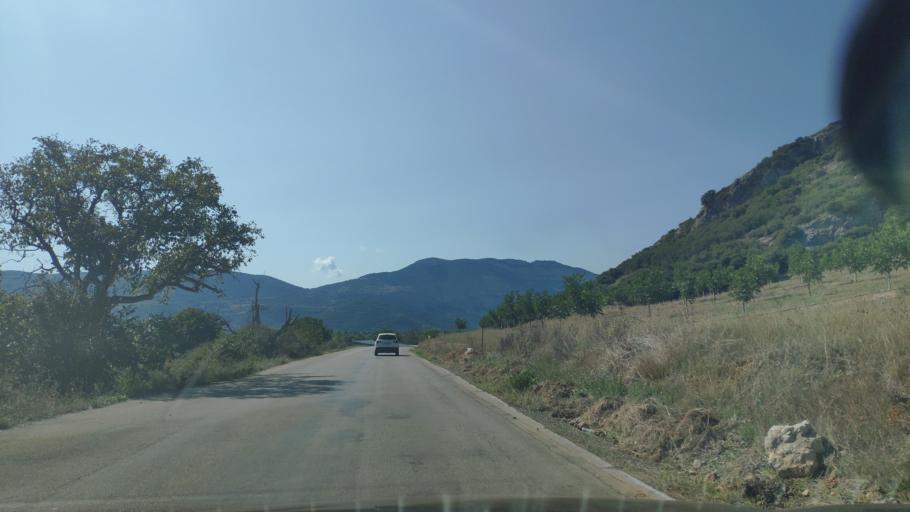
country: GR
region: Peloponnese
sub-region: Nomos Korinthias
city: Nemea
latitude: 37.9053
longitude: 22.5226
